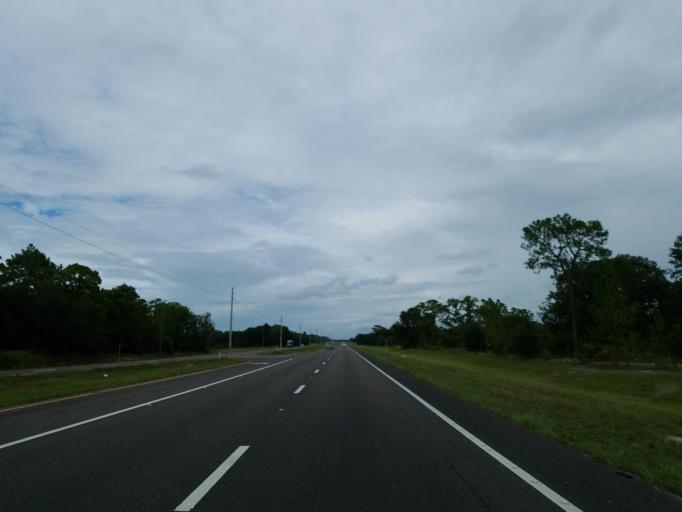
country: US
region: Florida
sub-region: Sumter County
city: Wildwood
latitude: 28.8678
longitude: -82.1472
